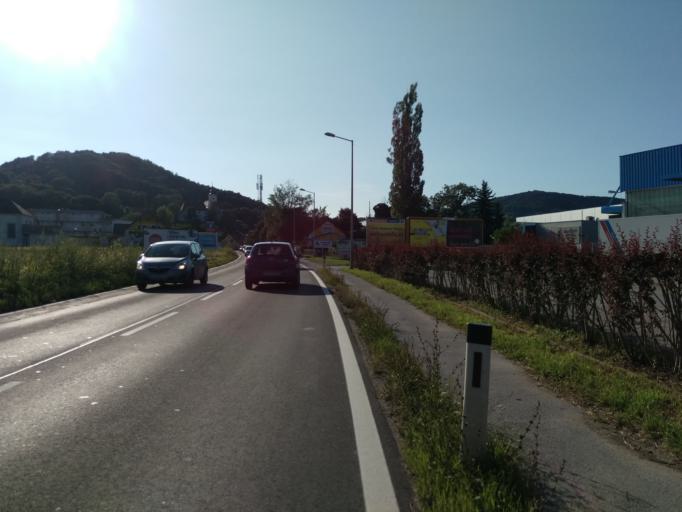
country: AT
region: Styria
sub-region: Politischer Bezirk Graz-Umgebung
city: Seiersberg
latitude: 47.0216
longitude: 15.4074
